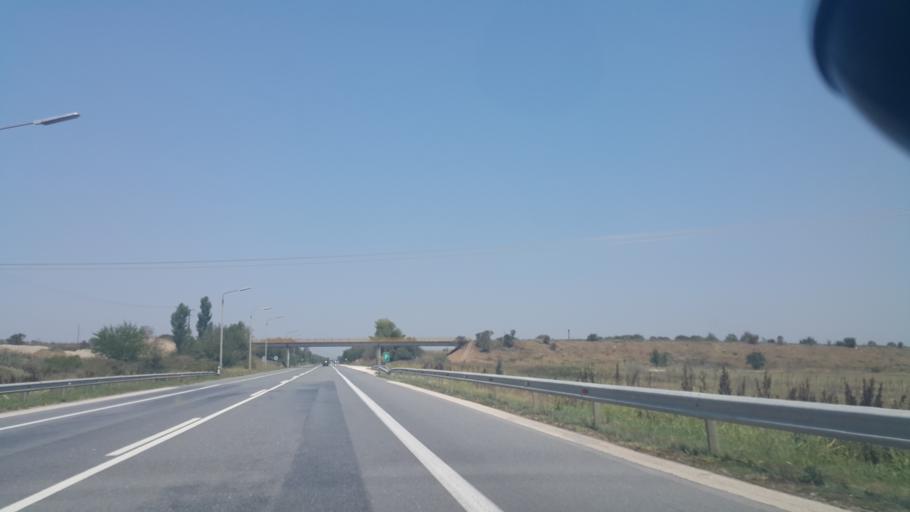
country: GR
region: Central Macedonia
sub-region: Nomos Thessalonikis
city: Prochoma
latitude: 40.8429
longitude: 22.6680
